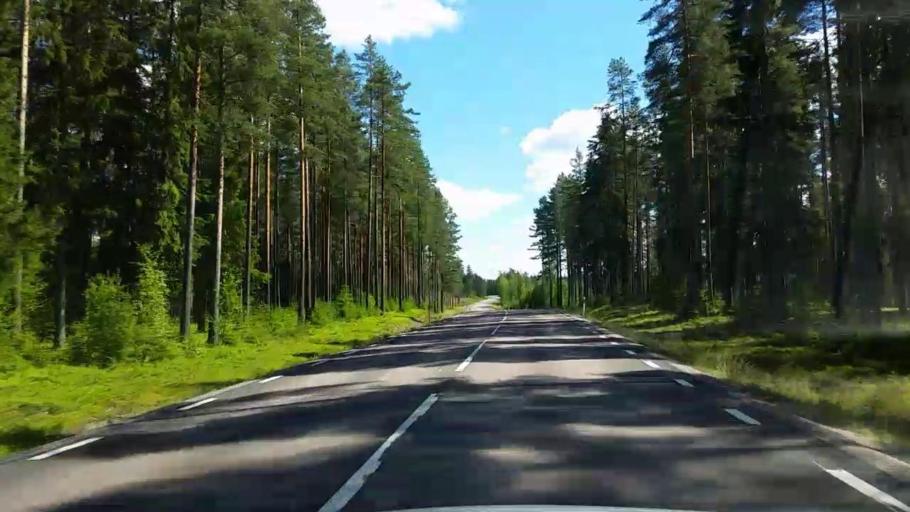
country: SE
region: Dalarna
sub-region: Faluns Kommun
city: Svardsjo
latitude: 60.7582
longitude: 15.7561
